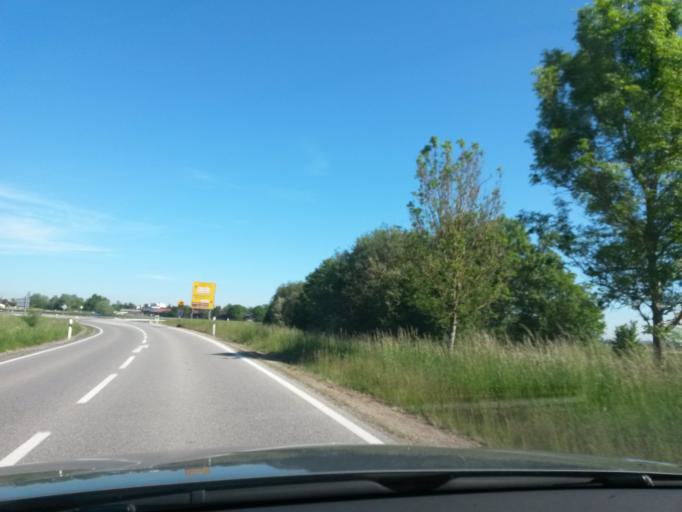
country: DE
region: Baden-Wuerttemberg
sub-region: Tuebingen Region
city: Bad Buchau
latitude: 48.0506
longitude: 9.6229
